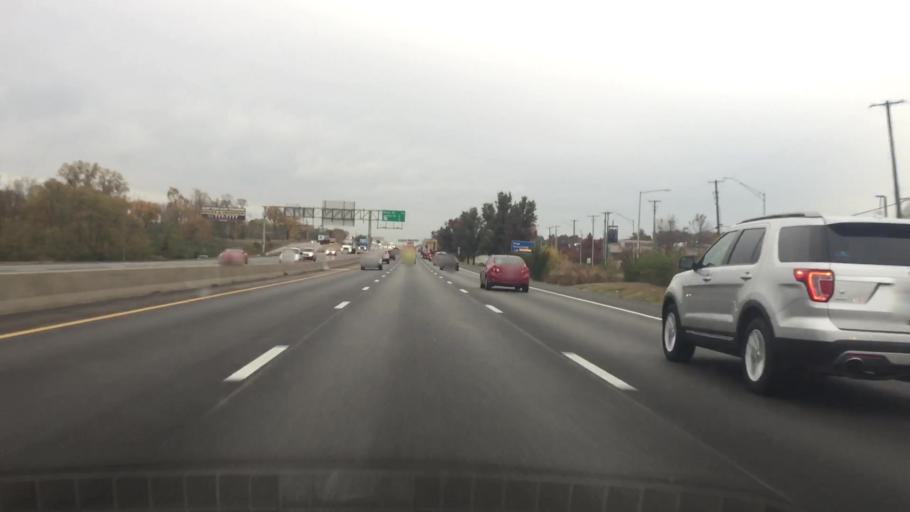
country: US
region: Missouri
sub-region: Jackson County
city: Grandview
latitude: 38.9051
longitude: -94.5242
